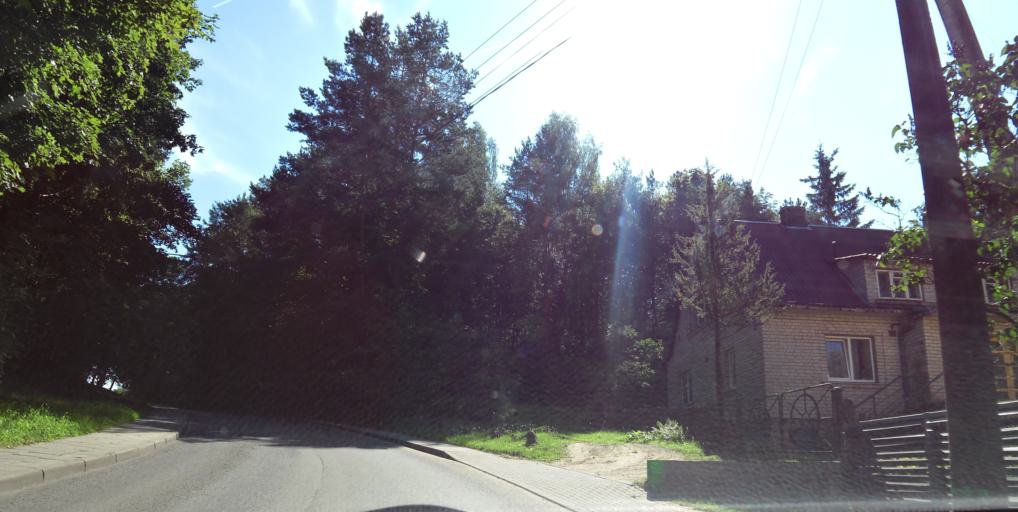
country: LT
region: Vilnius County
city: Rasos
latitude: 54.6900
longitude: 25.3169
